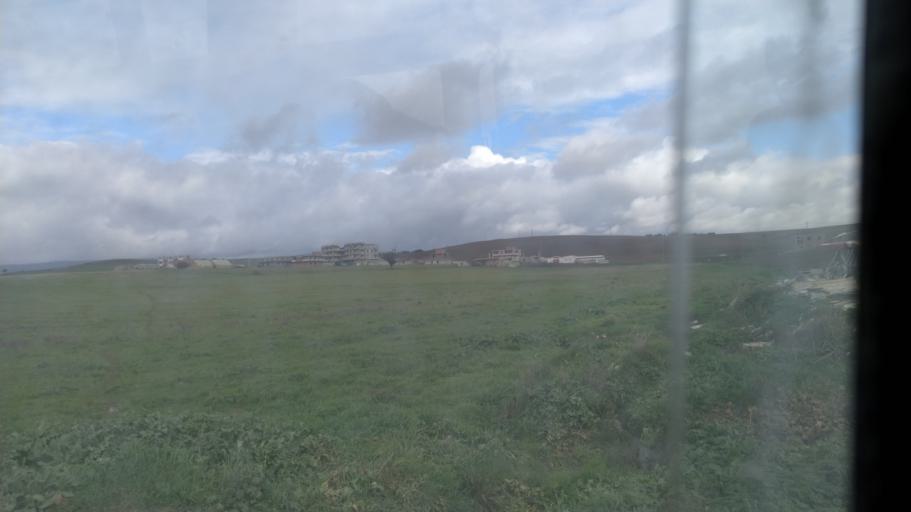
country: DZ
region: Constantine
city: El Khroub
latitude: 36.3010
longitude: 6.6979
